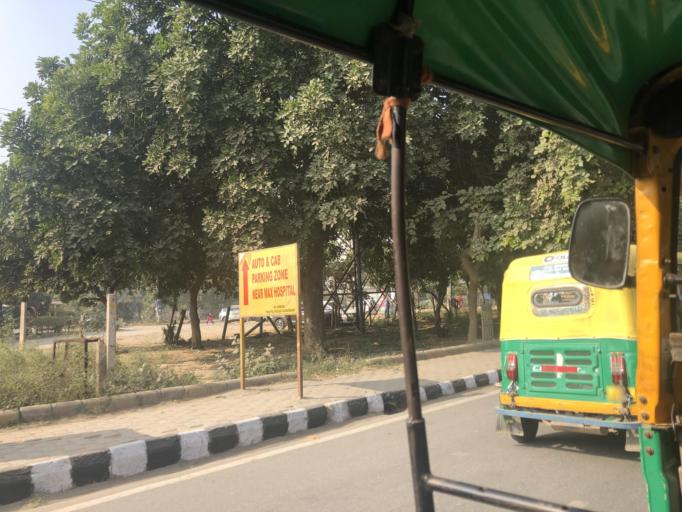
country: IN
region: Haryana
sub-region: Gurgaon
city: Gurgaon
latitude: 28.4533
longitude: 77.0749
